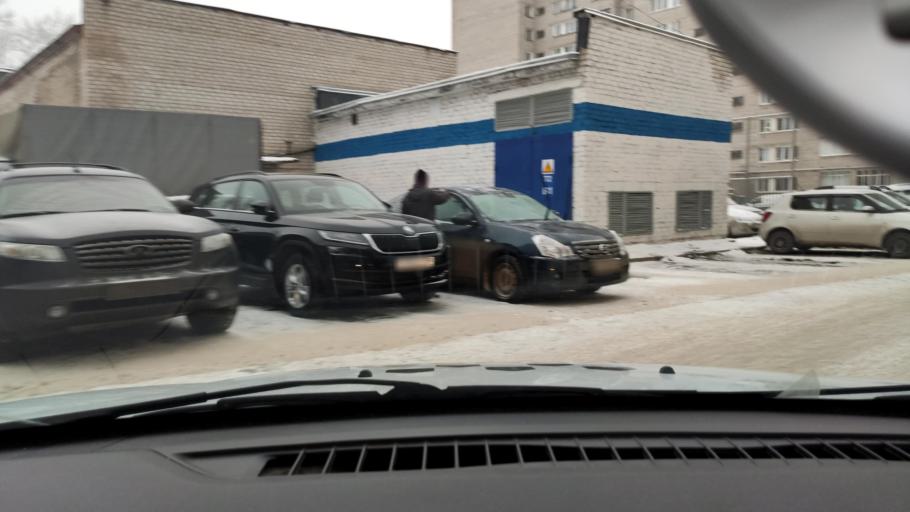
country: RU
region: Perm
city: Overyata
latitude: 58.0114
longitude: 55.9313
